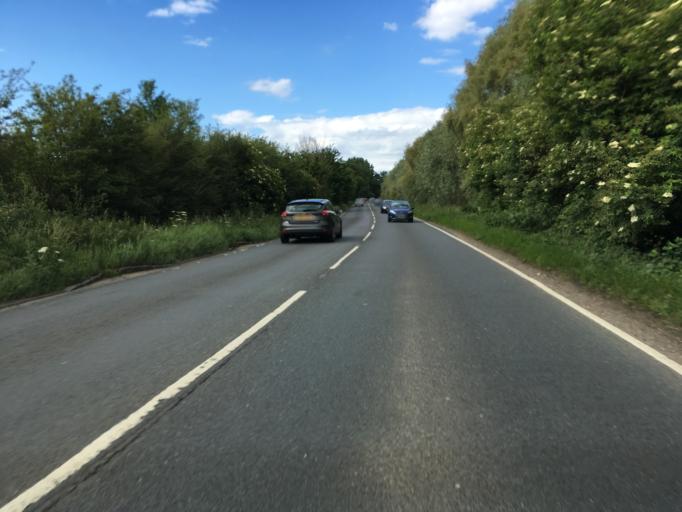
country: GB
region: England
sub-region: Buckinghamshire
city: Stewkley
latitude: 51.8617
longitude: -0.7634
